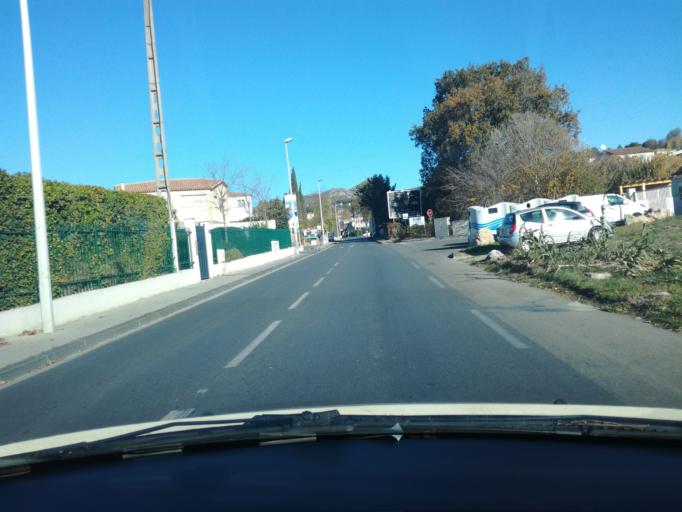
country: FR
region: Provence-Alpes-Cote d'Azur
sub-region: Departement des Bouches-du-Rhone
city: La Penne-sur-Huveaune
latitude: 43.3050
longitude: 5.5010
